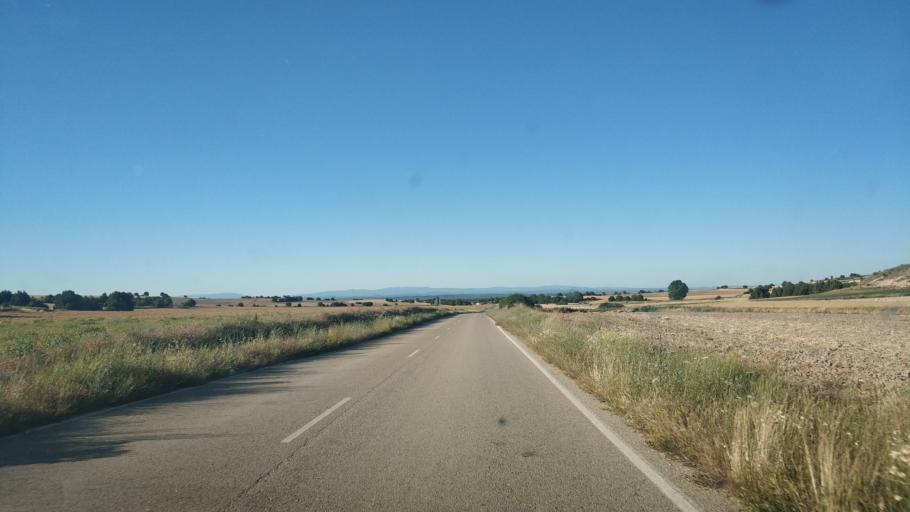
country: ES
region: Castille and Leon
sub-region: Provincia de Soria
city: San Esteban de Gormaz
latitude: 41.4793
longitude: -3.2152
